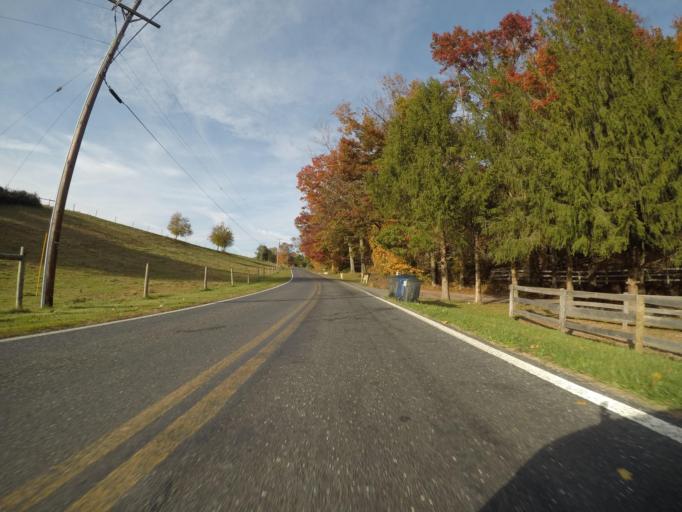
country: US
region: Maryland
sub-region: Carroll County
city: Hampstead
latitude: 39.5696
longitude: -76.9001
